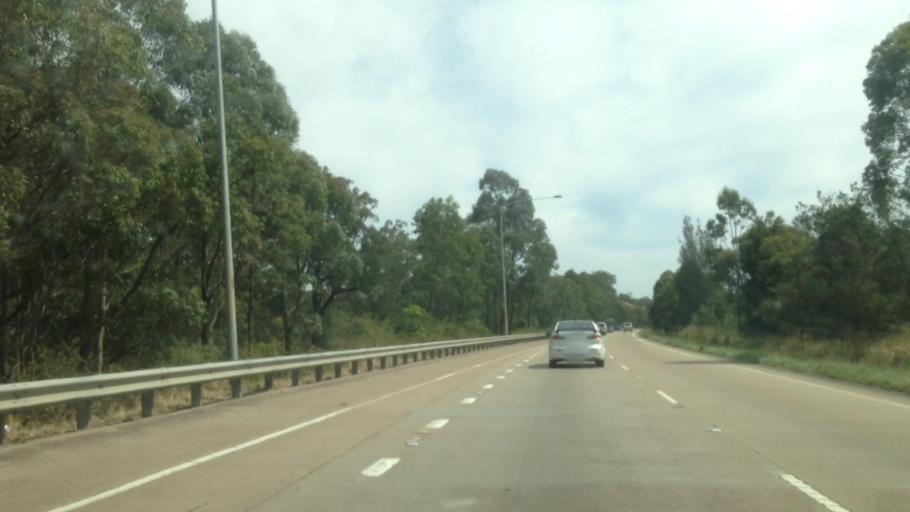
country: AU
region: New South Wales
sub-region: Lake Macquarie Shire
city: Holmesville
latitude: -32.8936
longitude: 151.5946
